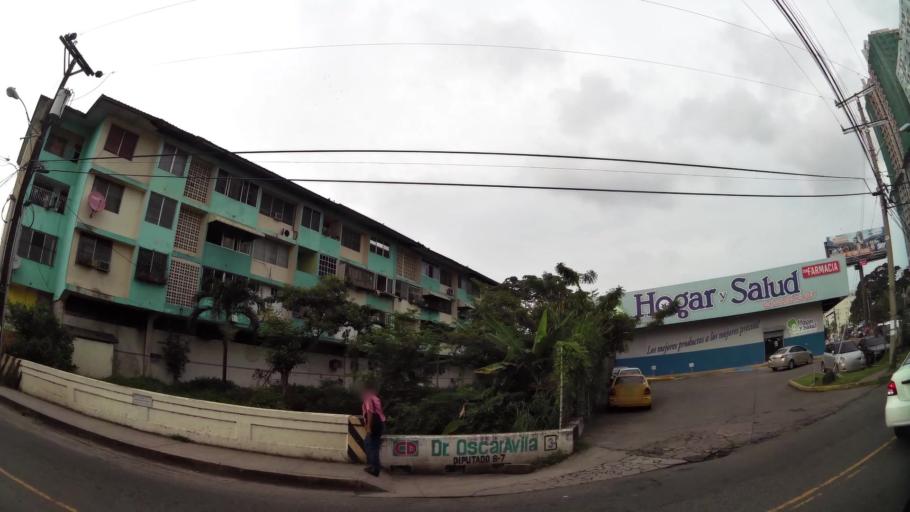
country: PA
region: Panama
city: Panama
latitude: 8.9985
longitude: -79.5187
